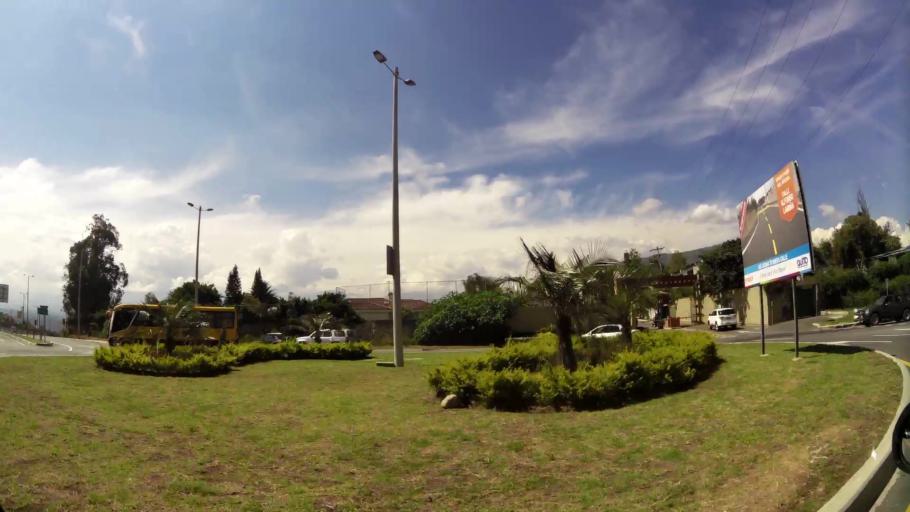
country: EC
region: Pichincha
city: Quito
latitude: -0.2117
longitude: -78.4406
